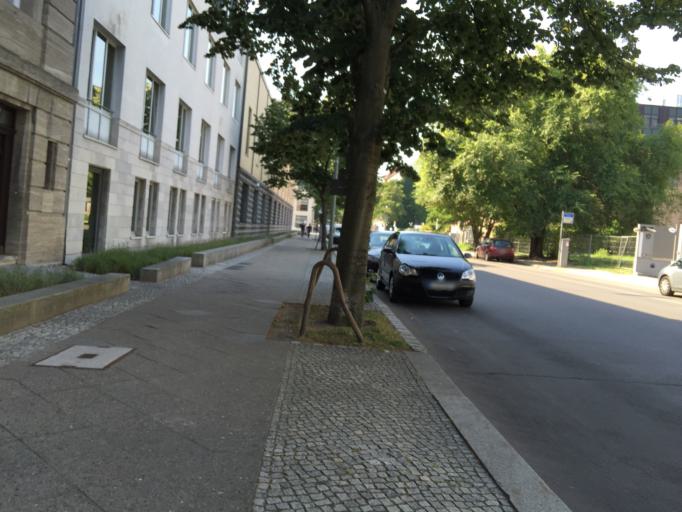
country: DE
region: Berlin
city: Tiergarten Bezirk
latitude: 52.5093
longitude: 13.3643
